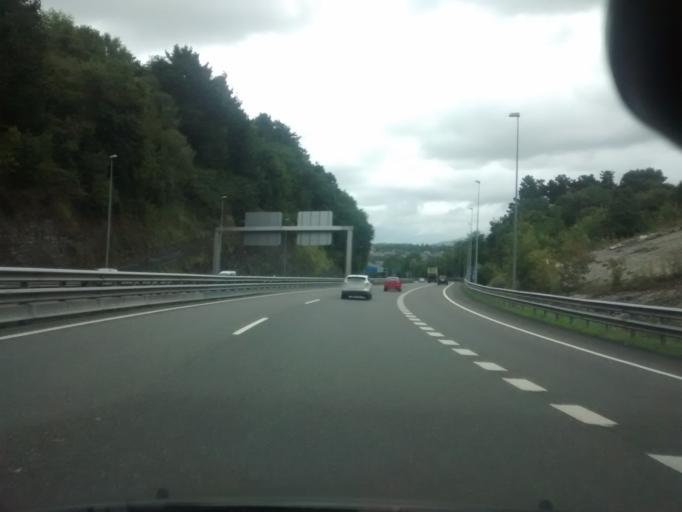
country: ES
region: Basque Country
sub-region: Provincia de Guipuzcoa
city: Lasarte
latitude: 43.2942
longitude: -2.0159
